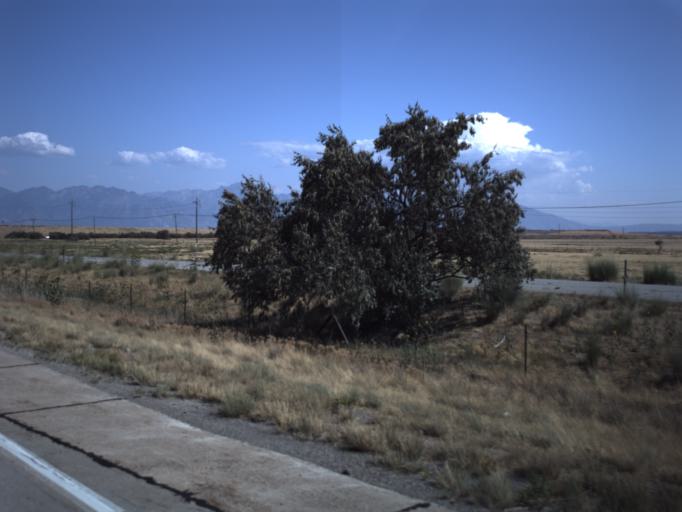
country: US
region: Utah
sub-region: Salt Lake County
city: Magna
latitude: 40.7708
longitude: -112.0706
